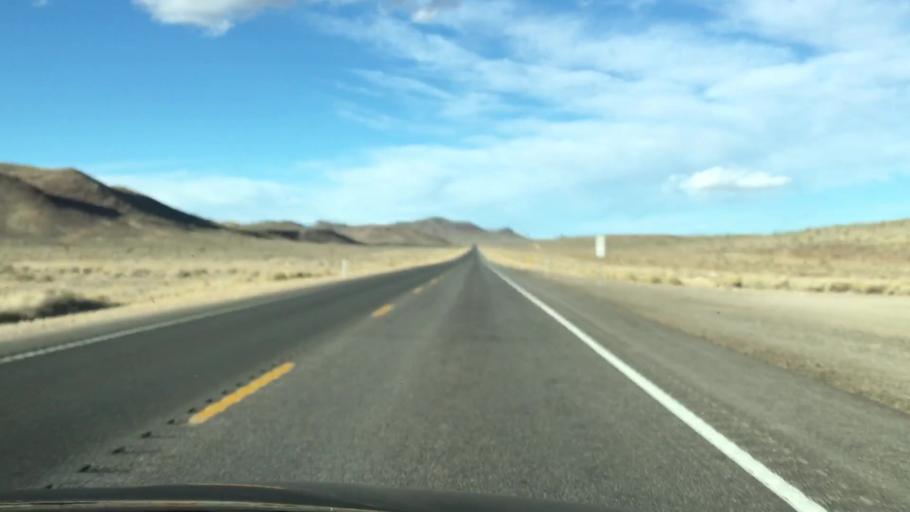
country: US
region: Nevada
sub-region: Esmeralda County
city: Goldfield
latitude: 37.6263
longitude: -117.2187
